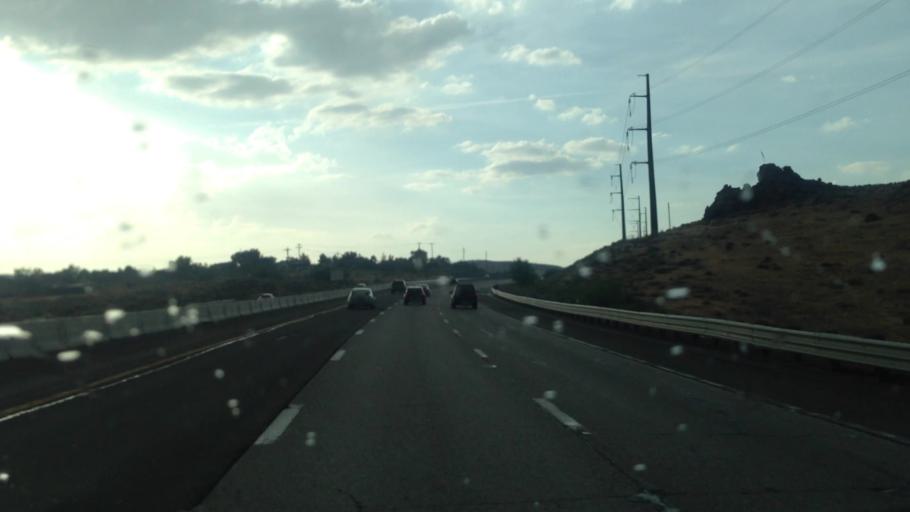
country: US
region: Nevada
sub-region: Washoe County
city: Golden Valley
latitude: 39.5795
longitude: -119.8160
